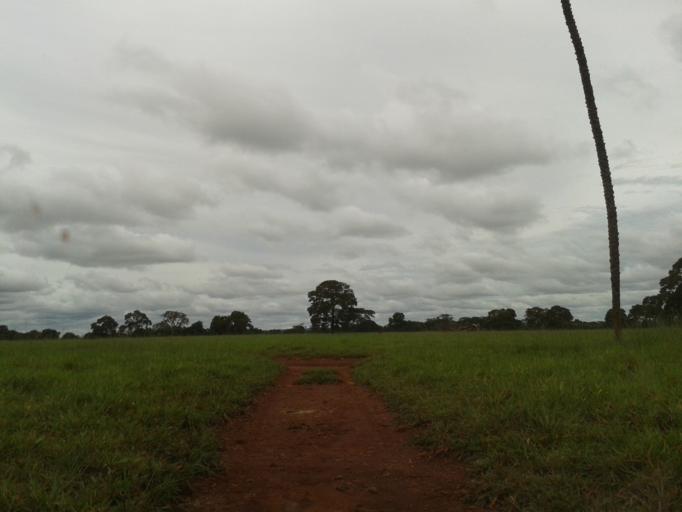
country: BR
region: Minas Gerais
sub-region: Capinopolis
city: Capinopolis
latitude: -18.7792
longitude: -49.7727
